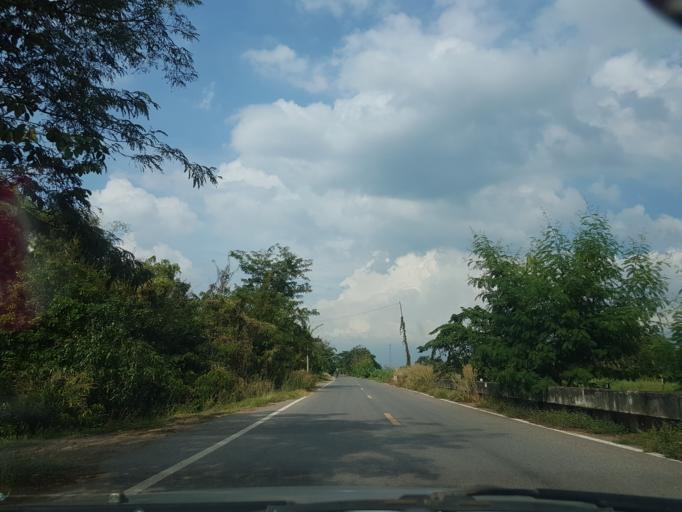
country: TH
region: Sara Buri
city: Nong Khae
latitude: 14.2341
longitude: 100.8914
